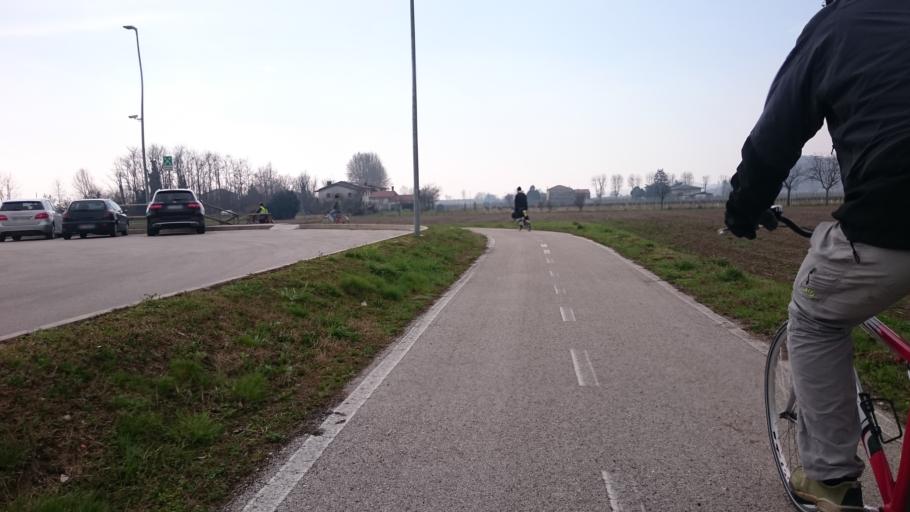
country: IT
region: Veneto
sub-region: Provincia di Vicenza
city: Lumignano
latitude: 45.4575
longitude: 11.6037
